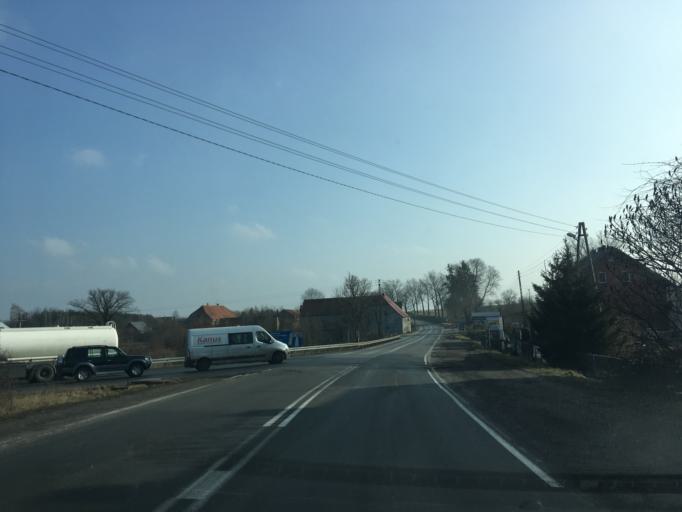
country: PL
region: Lower Silesian Voivodeship
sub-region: Powiat legnicki
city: Chojnow
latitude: 51.2632
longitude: 15.9481
